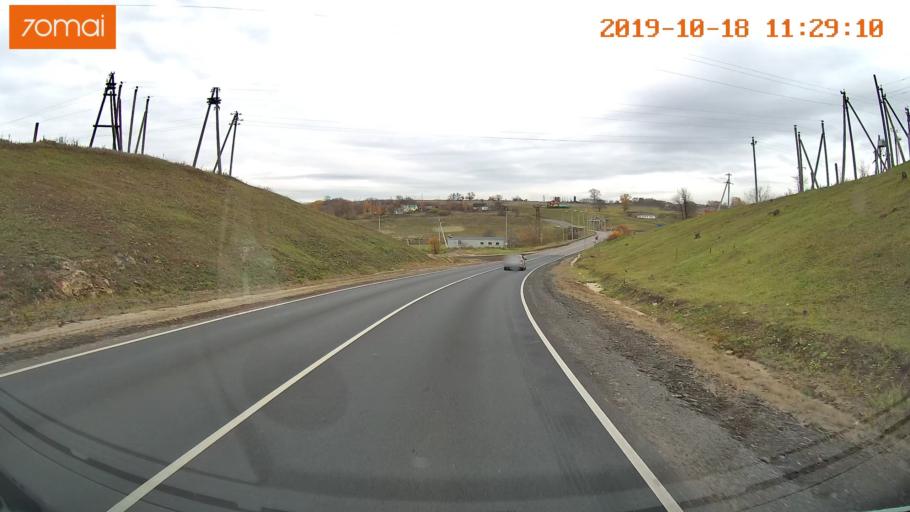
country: RU
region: Rjazan
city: Oktyabr'skiy
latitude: 54.1575
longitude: 38.6733
